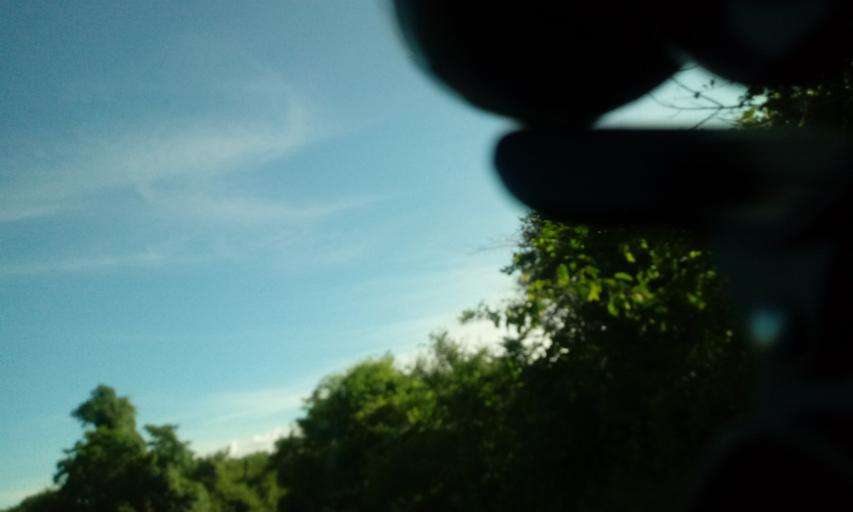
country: BR
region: Bahia
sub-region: Riacho De Santana
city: Riacho de Santana
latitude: -13.8499
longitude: -42.7699
